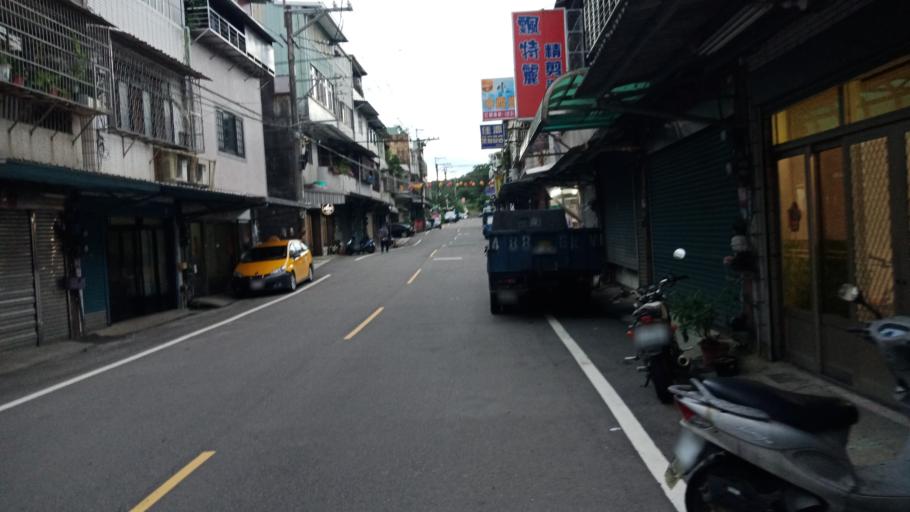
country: TW
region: Taiwan
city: Daxi
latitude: 24.8716
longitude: 121.1982
